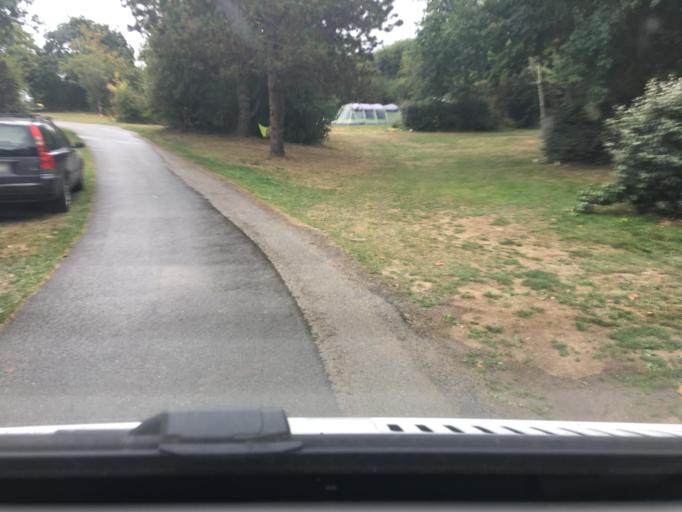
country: FR
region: Brittany
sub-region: Departement du Finistere
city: Beuzec-Cap-Sizun
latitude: 48.0834
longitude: -4.4821
